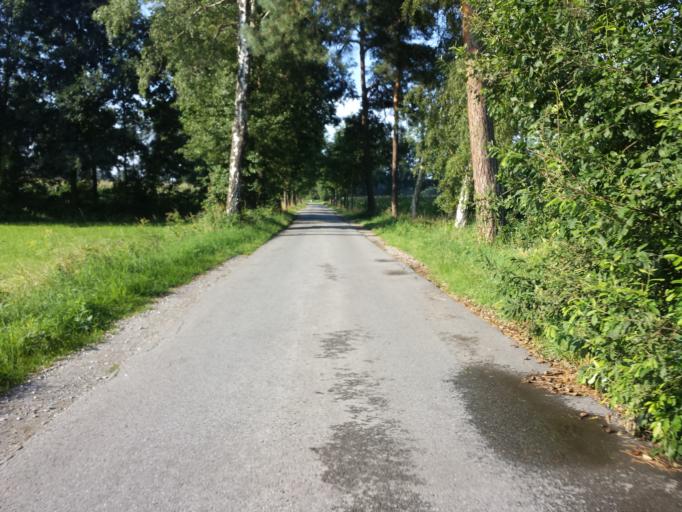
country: DE
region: North Rhine-Westphalia
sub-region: Regierungsbezirk Detmold
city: Guetersloh
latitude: 51.9155
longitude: 8.3389
